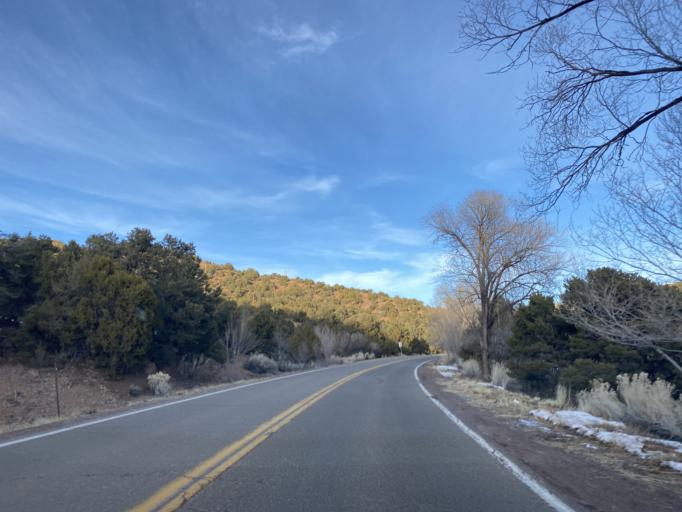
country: US
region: New Mexico
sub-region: Santa Fe County
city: Santa Fe
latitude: 35.7042
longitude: -105.9051
